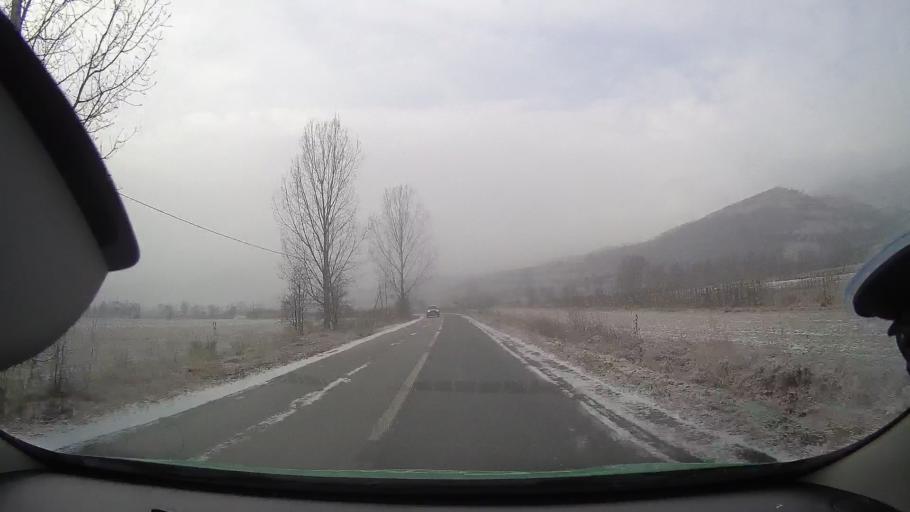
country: RO
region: Alba
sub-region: Comuna Rimetea
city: Rimetea
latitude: 46.4085
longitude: 23.5587
